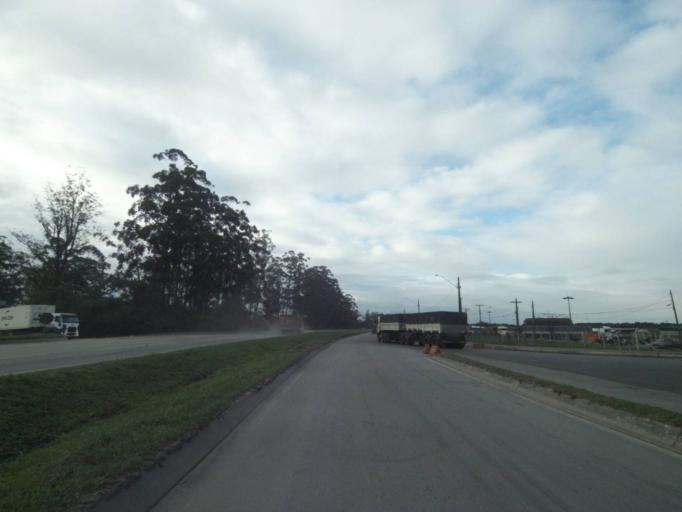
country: BR
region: Parana
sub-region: Paranagua
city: Paranagua
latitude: -25.5401
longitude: -48.5584
